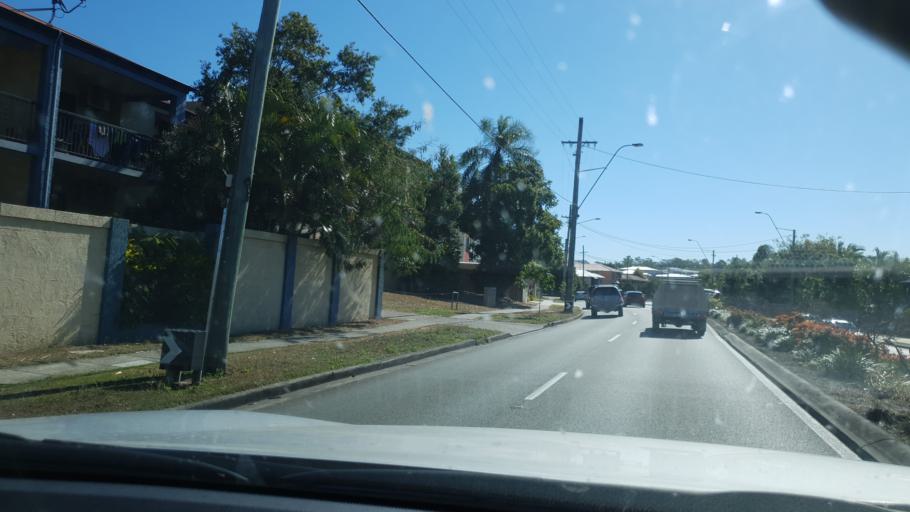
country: AU
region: Queensland
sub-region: Brisbane
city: Everton Park
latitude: -27.4052
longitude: 152.9899
